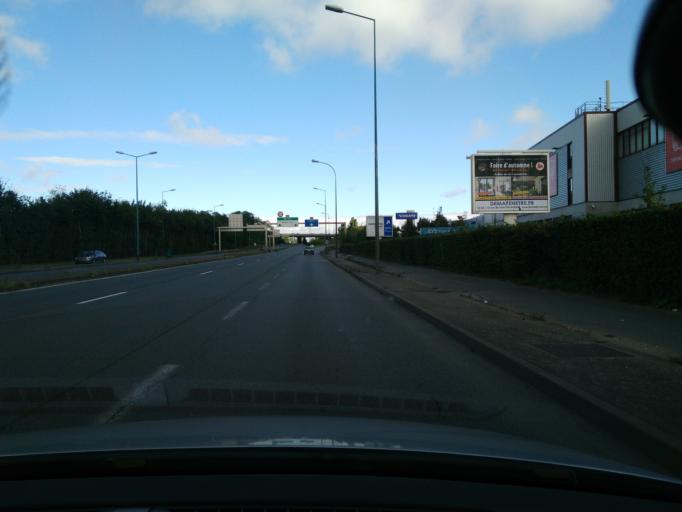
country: FR
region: Ile-de-France
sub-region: Departement de l'Essonne
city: Massy
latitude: 48.7209
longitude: 2.2992
